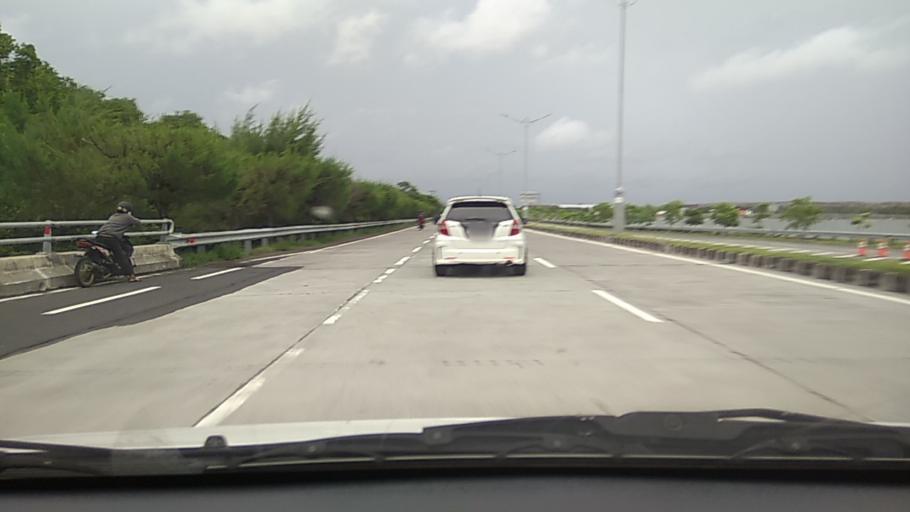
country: ID
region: Bali
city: Karyadharma
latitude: -8.7317
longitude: 115.2123
